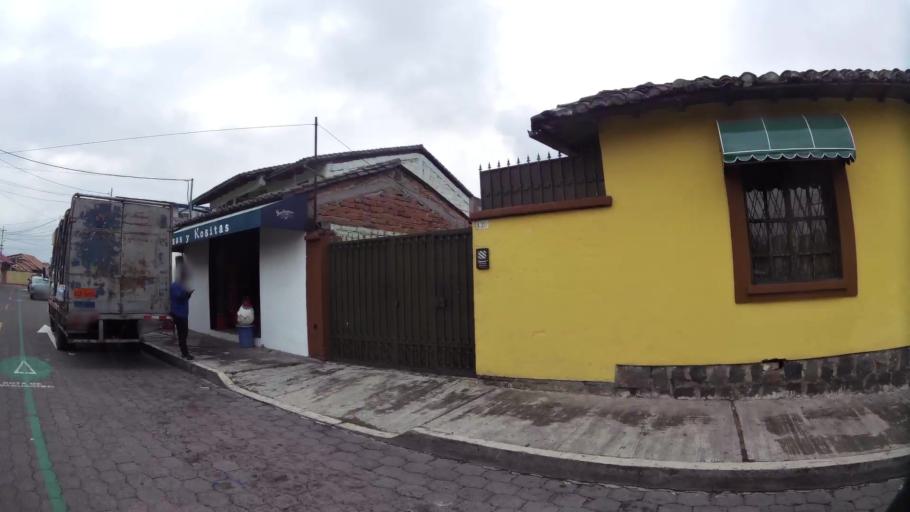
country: EC
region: Pichincha
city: Sangolqui
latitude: -0.3052
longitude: -78.4582
